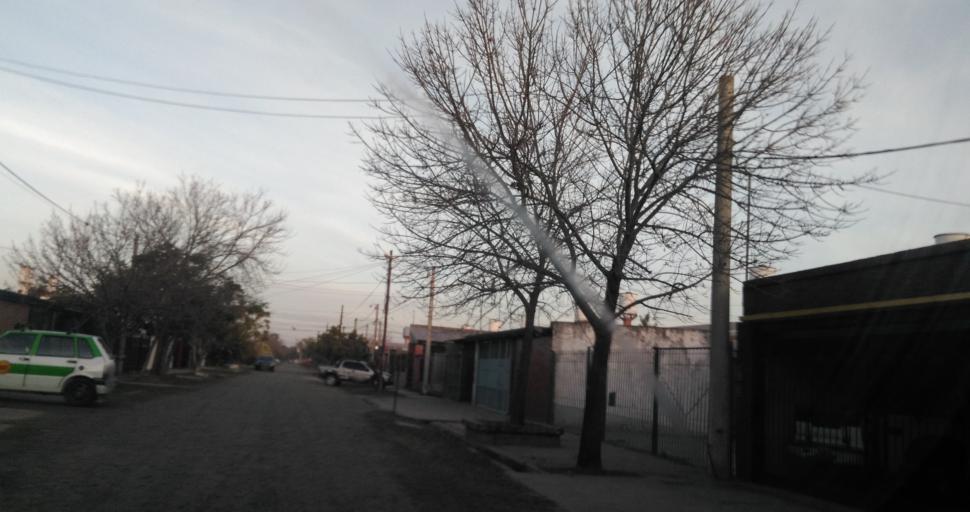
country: AR
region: Chaco
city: Resistencia
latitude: -27.4638
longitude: -59.0144
